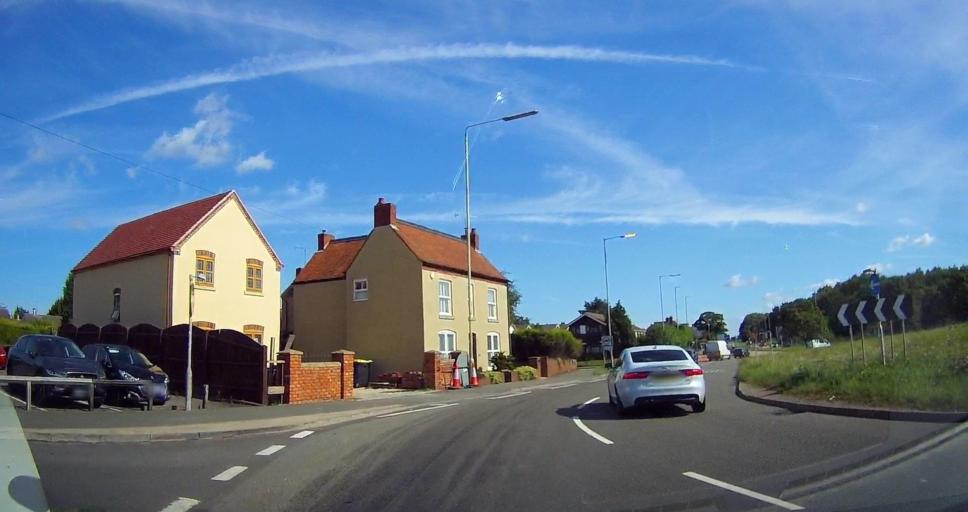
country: GB
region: England
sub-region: Staffordshire
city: Norton Canes
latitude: 52.6559
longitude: -1.9517
